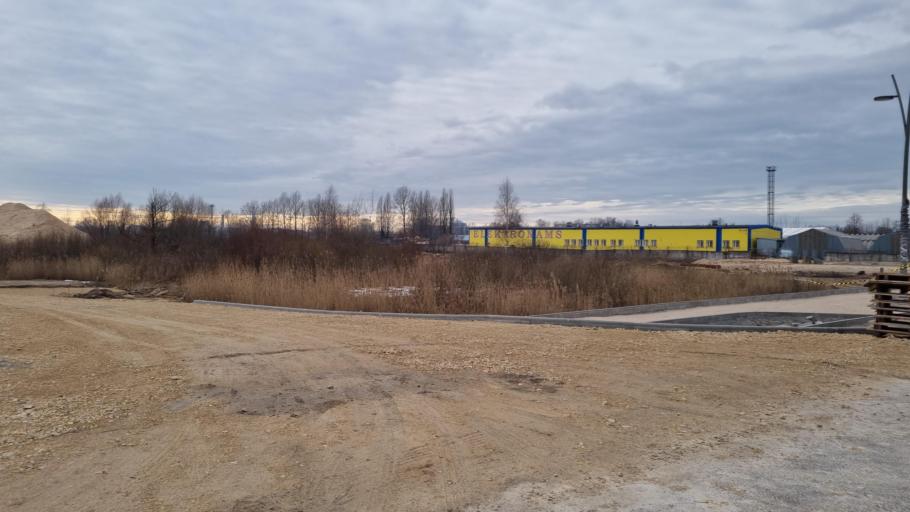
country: LV
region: Riga
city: Riga
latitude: 56.9731
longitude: 24.1199
